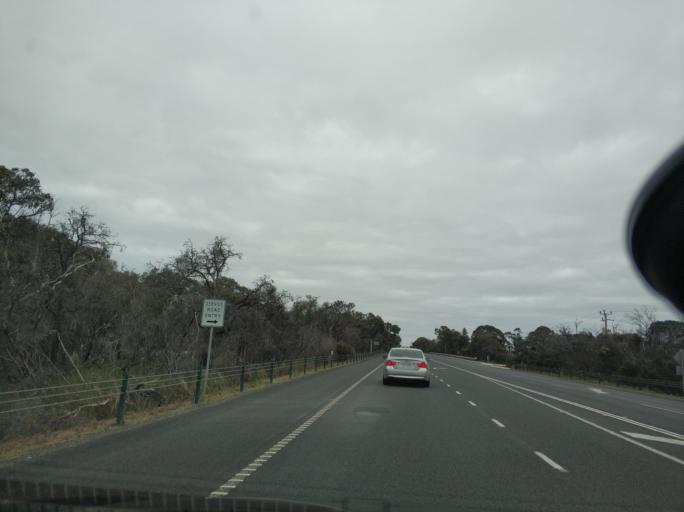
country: AU
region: Victoria
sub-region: Surf Coast
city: Anglesea
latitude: -38.3768
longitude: 144.2163
